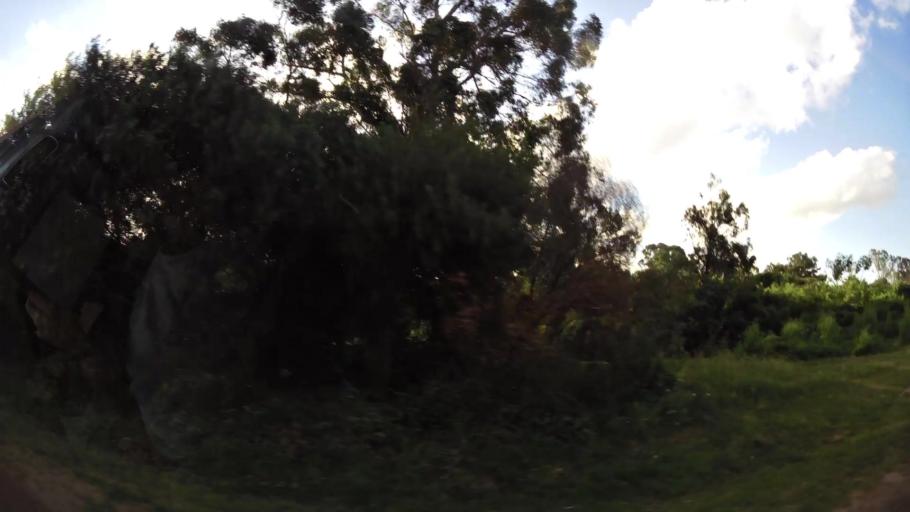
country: UY
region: Montevideo
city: Montevideo
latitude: -34.8959
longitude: -56.2613
